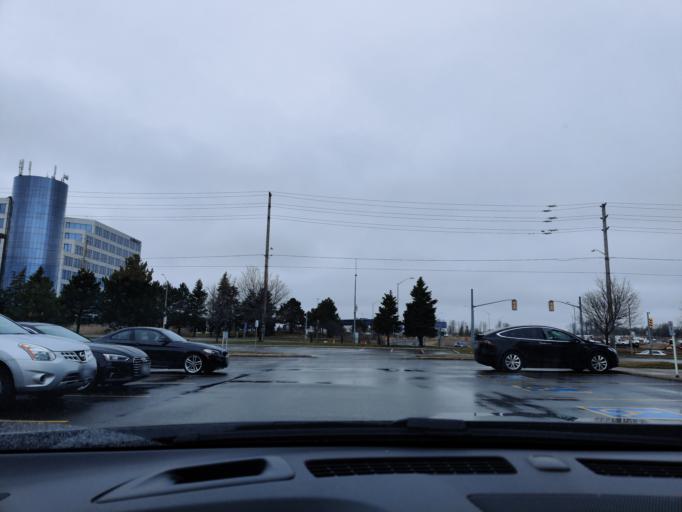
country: CA
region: Ontario
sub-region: York
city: Richmond Hill
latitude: 43.8640
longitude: -79.3772
